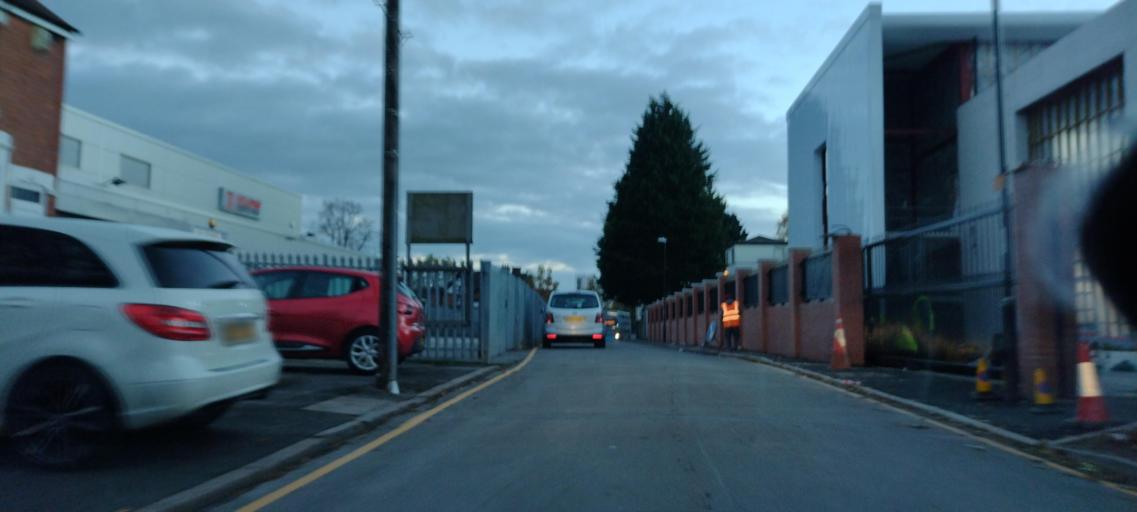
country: GB
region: England
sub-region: Coventry
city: Coventry
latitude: 52.4168
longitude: -1.5150
